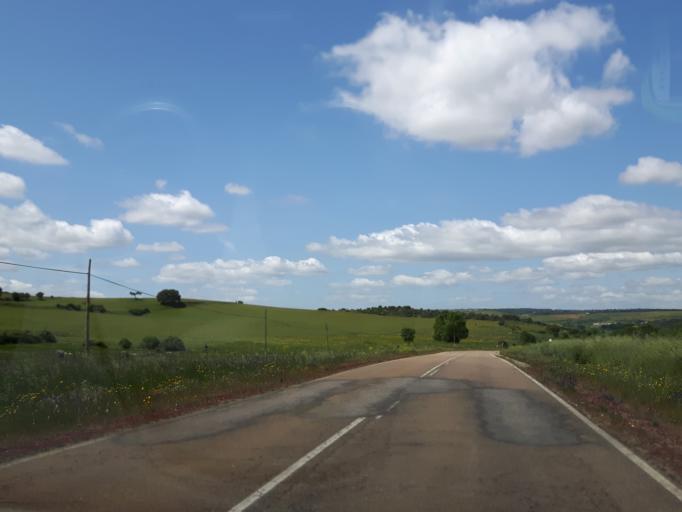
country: ES
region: Castille and Leon
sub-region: Provincia de Salamanca
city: Villar de Ciervo
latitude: 40.7249
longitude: -6.7596
